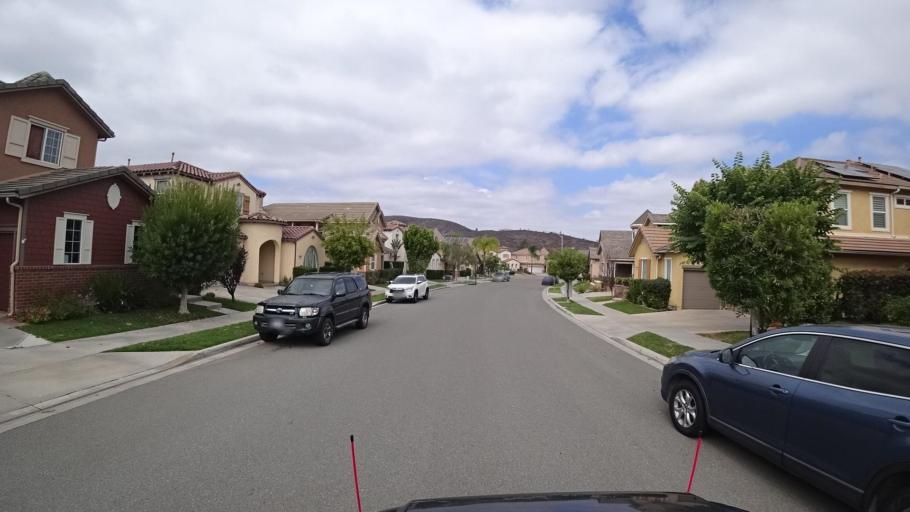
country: US
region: California
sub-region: San Diego County
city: Fairbanks Ranch
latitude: 33.0232
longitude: -117.1182
